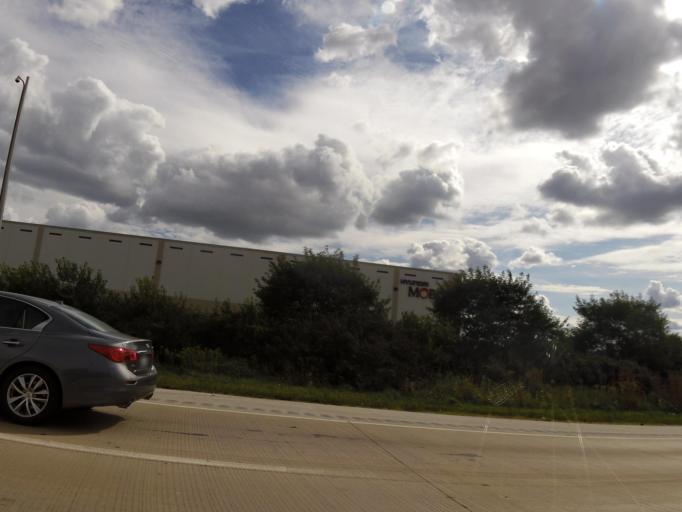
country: US
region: Illinois
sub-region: Kane County
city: North Aurora
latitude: 41.7951
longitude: -88.3585
